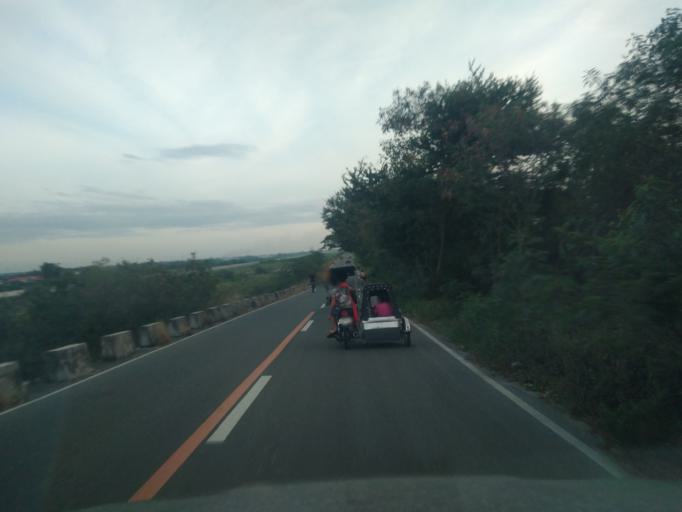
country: PH
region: Central Luzon
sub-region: Province of Pampanga
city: Santa Rita
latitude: 15.0199
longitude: 120.6201
